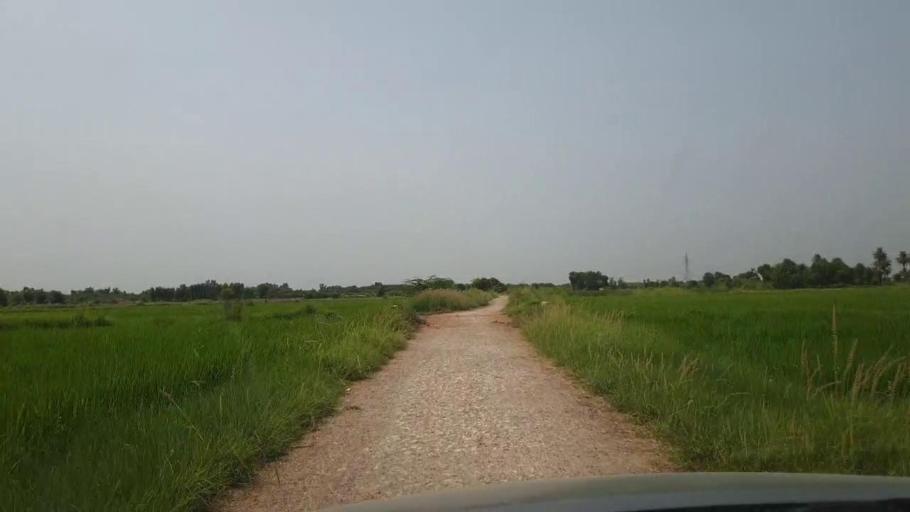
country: PK
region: Sindh
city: Madeji
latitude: 27.7895
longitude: 68.5384
